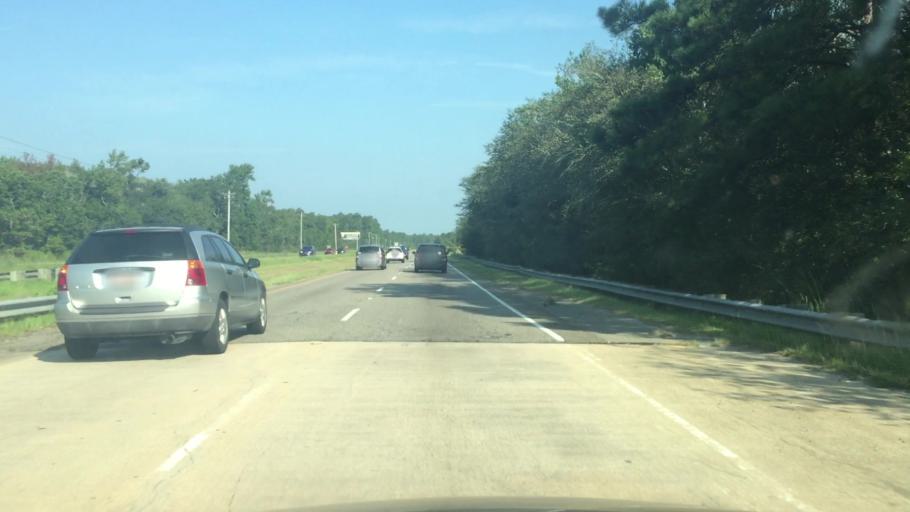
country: US
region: South Carolina
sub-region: Horry County
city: North Myrtle Beach
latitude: 33.9093
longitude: -78.7104
